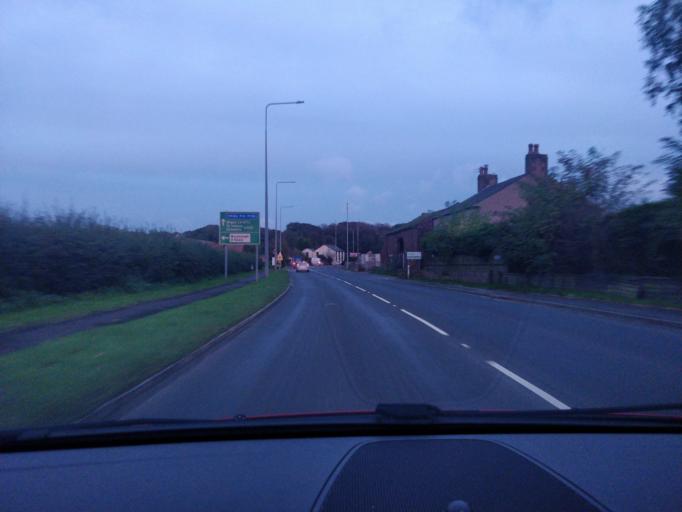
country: GB
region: England
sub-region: Lancashire
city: Ormskirk
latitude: 53.6114
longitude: -2.9374
